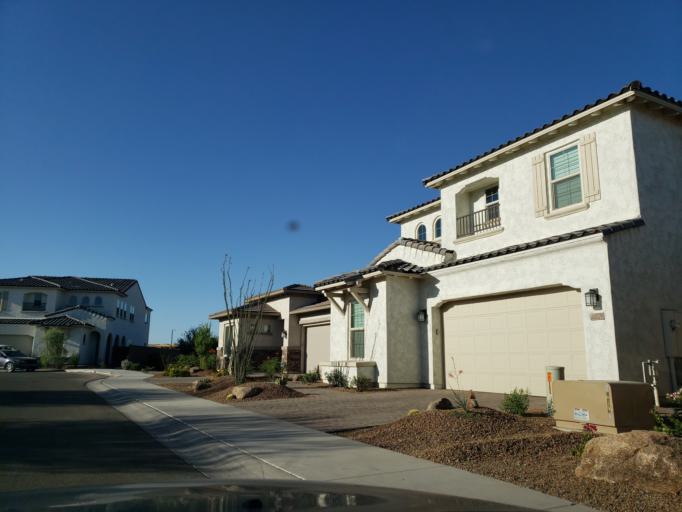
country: US
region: Arizona
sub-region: Maricopa County
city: Cave Creek
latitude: 33.6866
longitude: -112.0100
